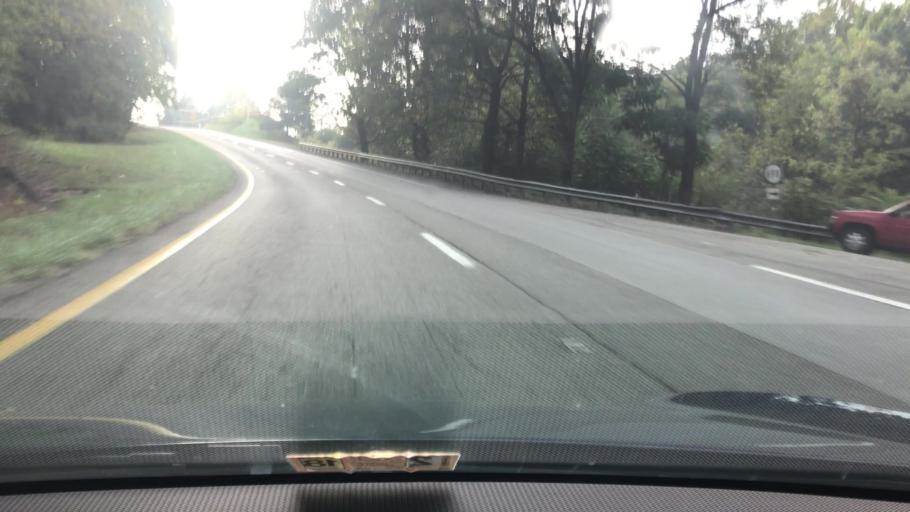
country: US
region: Virginia
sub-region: Botetourt County
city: Blue Ridge
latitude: 37.3881
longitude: -79.7404
